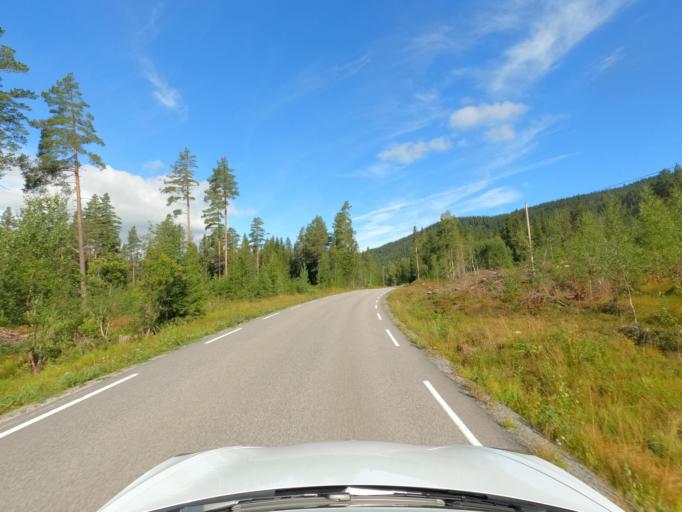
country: NO
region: Buskerud
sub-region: Nore og Uvdal
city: Rodberg
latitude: 60.1021
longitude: 8.7513
